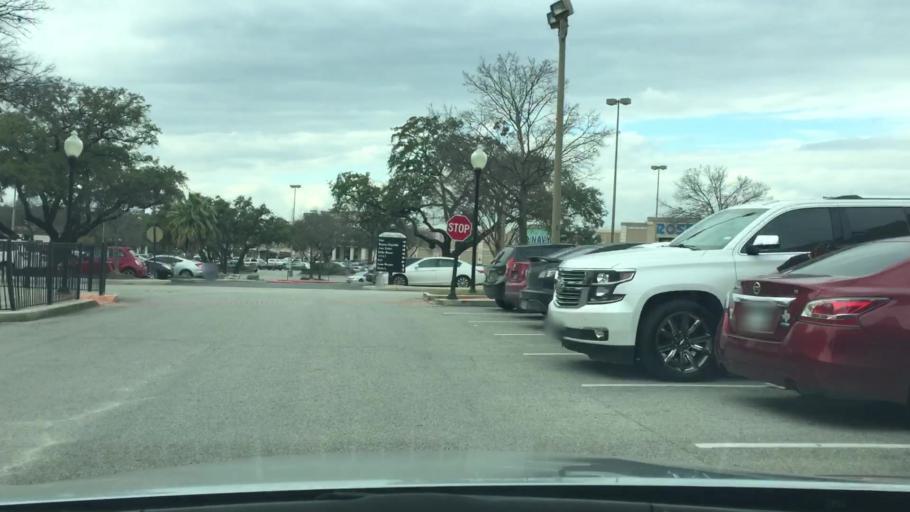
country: US
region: Texas
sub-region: Bexar County
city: Shavano Park
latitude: 29.5489
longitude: -98.5822
